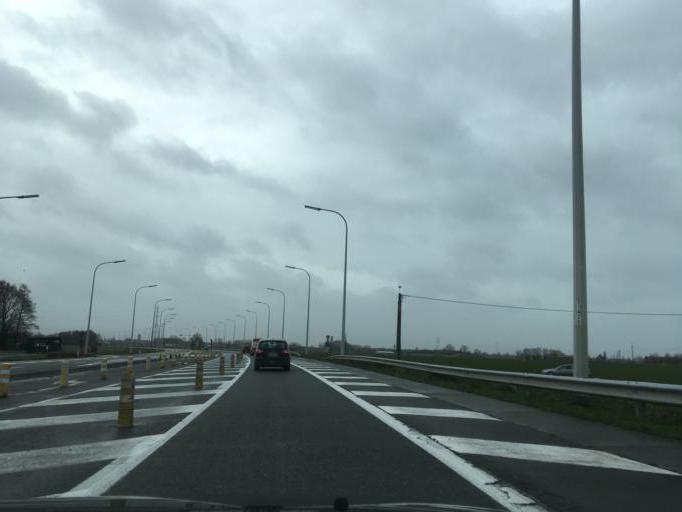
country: BE
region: Flanders
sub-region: Provincie West-Vlaanderen
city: Hooglede
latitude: 50.9745
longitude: 3.1050
